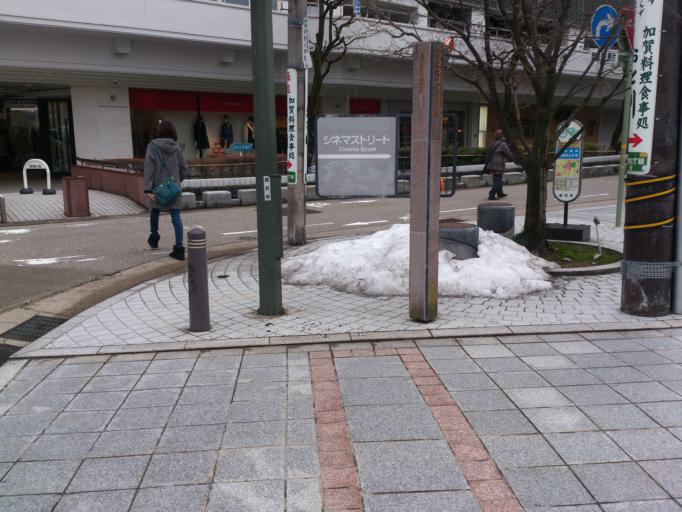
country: JP
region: Ishikawa
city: Kanazawa-shi
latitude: 36.5627
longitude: 136.6525
